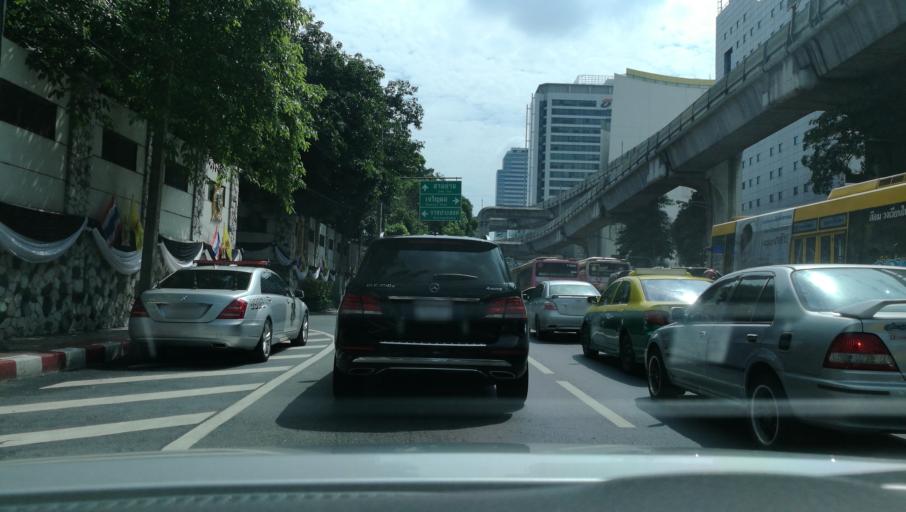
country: TH
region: Bangkok
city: Ratchathewi
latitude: 13.7482
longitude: 100.5311
